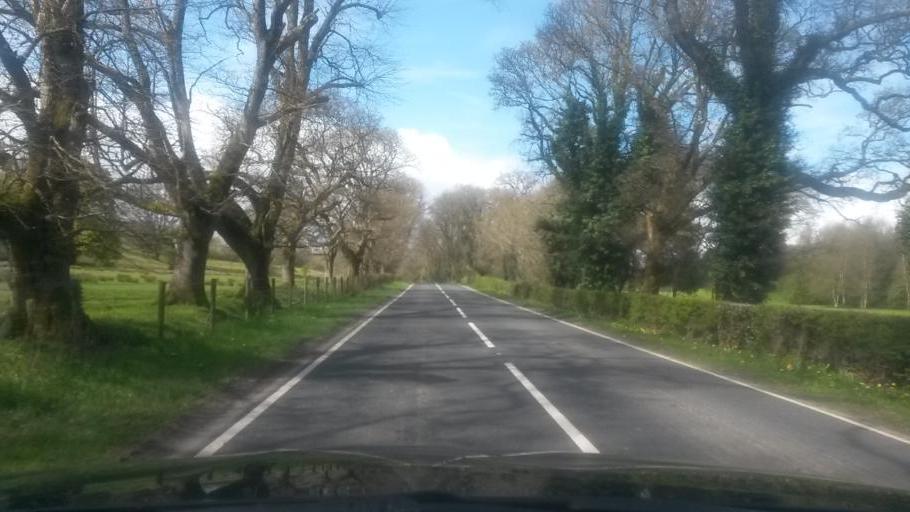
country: GB
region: Northern Ireland
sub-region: Fermanagh District
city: Enniskillen
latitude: 54.3889
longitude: -7.6986
